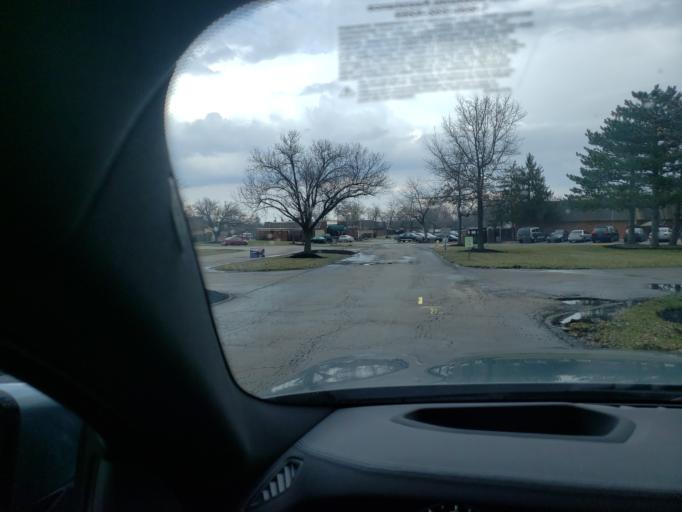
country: US
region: Ohio
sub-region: Hamilton County
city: Springdale
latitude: 39.2792
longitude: -84.4825
